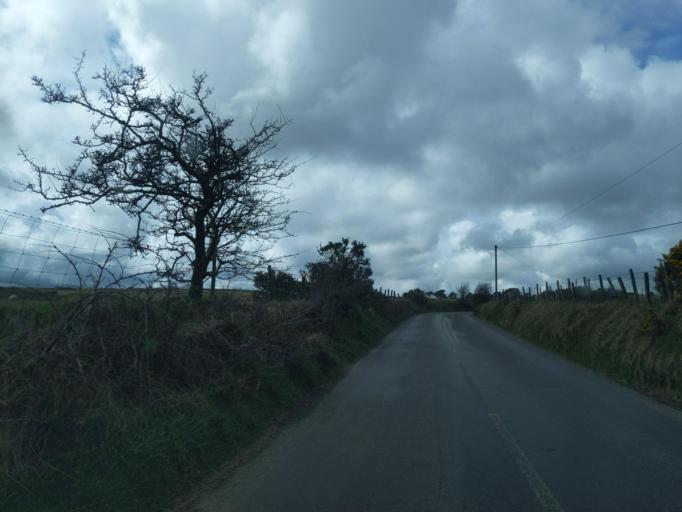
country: GB
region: England
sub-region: Cornwall
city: Camelford
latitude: 50.6244
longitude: -4.5897
